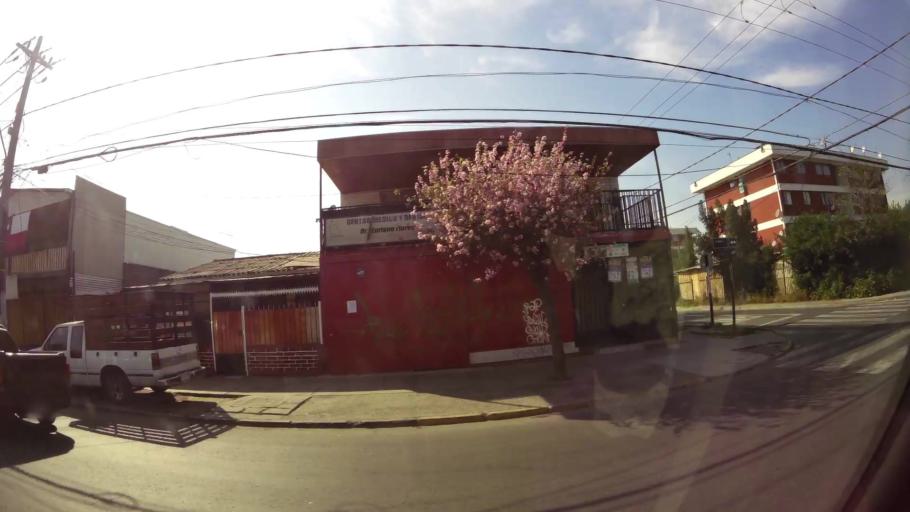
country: CL
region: Santiago Metropolitan
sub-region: Provincia de Santiago
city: Lo Prado
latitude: -33.4458
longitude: -70.7539
